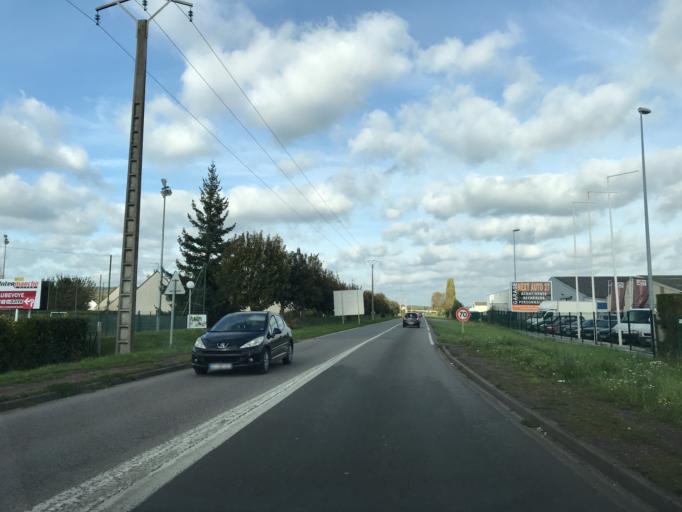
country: FR
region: Haute-Normandie
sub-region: Departement de l'Eure
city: Gaillon
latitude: 49.1635
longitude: 1.3488
